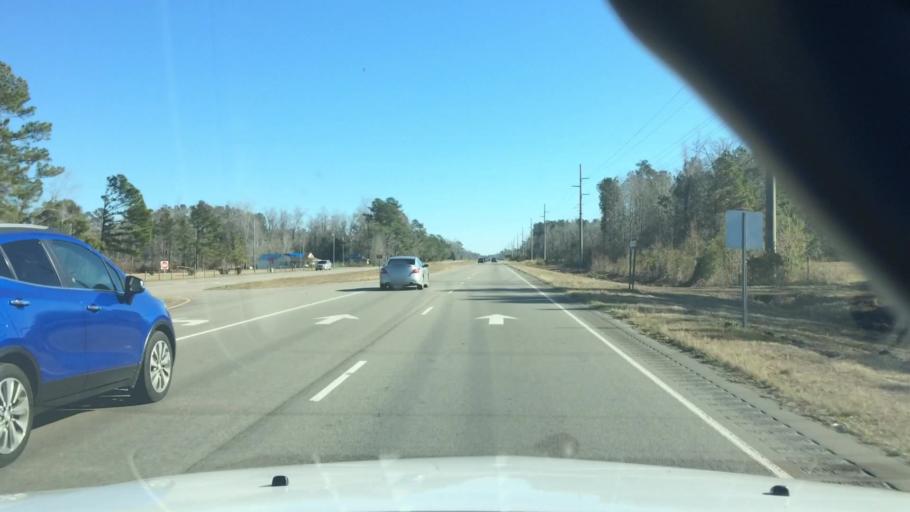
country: US
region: North Carolina
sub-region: Brunswick County
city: Shallotte
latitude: 34.0029
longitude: -78.3137
